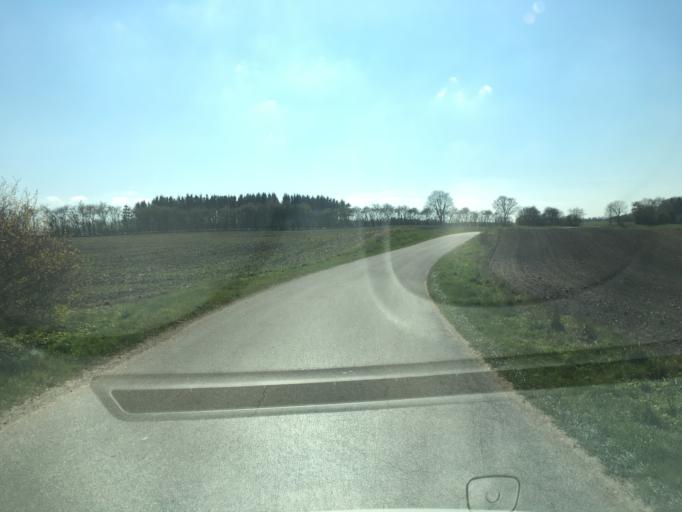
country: DK
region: South Denmark
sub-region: Aabenraa Kommune
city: Krusa
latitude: 54.9242
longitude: 9.4774
